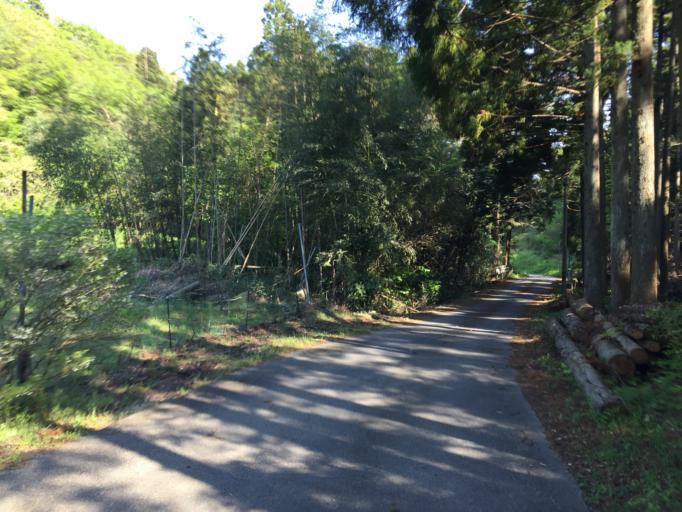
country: JP
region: Fukushima
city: Iwaki
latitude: 37.0553
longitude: 140.7912
